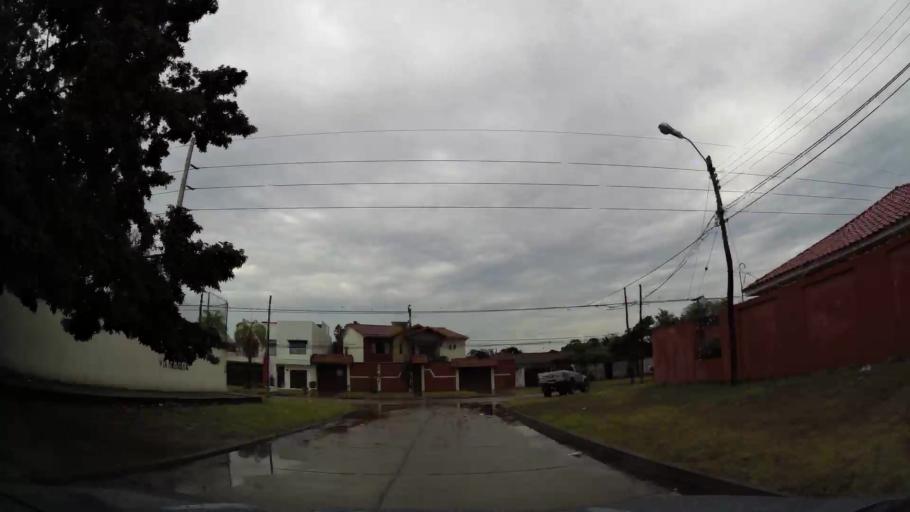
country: BO
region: Santa Cruz
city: Santa Cruz de la Sierra
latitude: -17.8078
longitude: -63.1694
